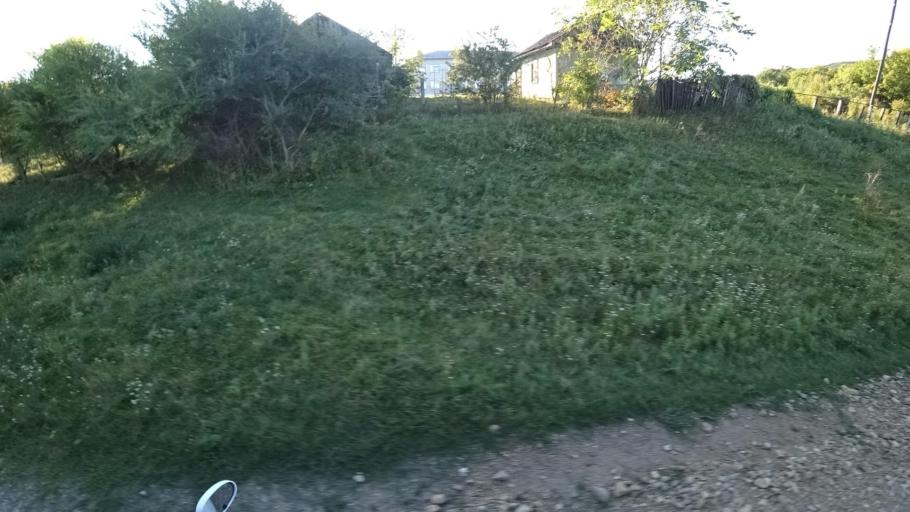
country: RU
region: Primorskiy
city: Kirovskiy
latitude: 44.8264
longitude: 133.5748
